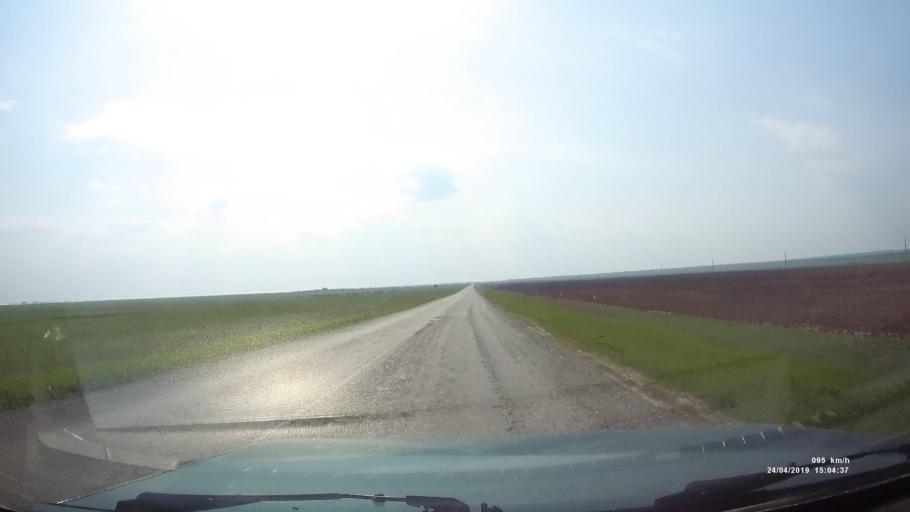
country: RU
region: Rostov
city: Remontnoye
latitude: 46.5617
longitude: 43.4661
